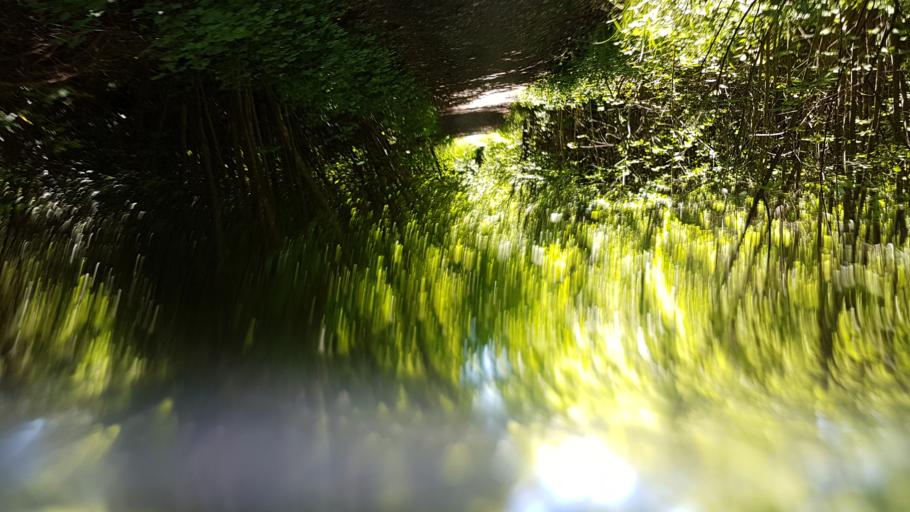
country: CH
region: Bern
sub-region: Thun District
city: Thun
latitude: 46.7074
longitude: 7.5966
